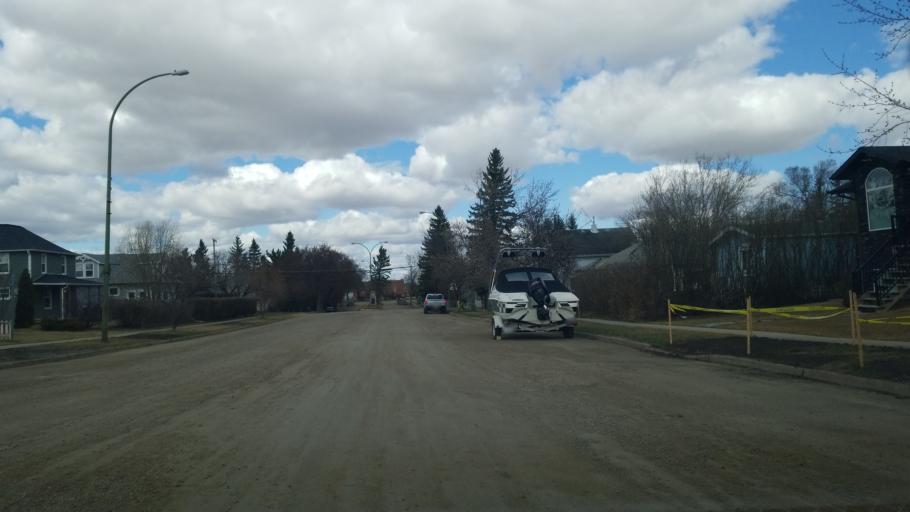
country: CA
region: Saskatchewan
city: Lloydminster
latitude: 53.1260
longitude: -109.6164
